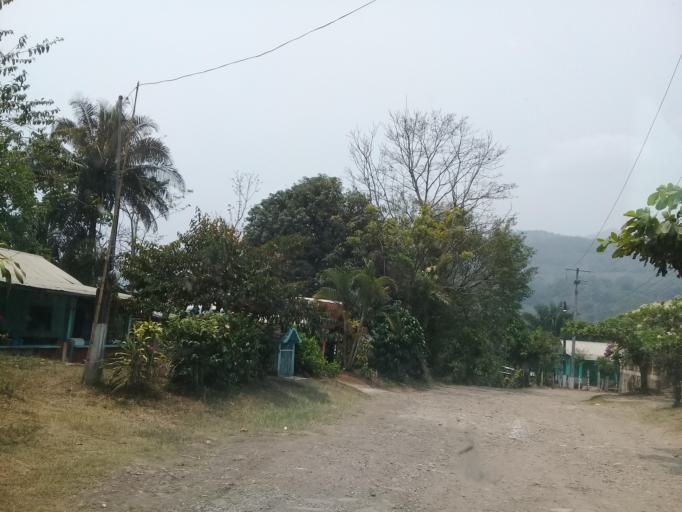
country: MX
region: Veracruz
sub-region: Tezonapa
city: Laguna Chica (Pueblo Nuevo)
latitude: 18.5456
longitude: -96.7352
